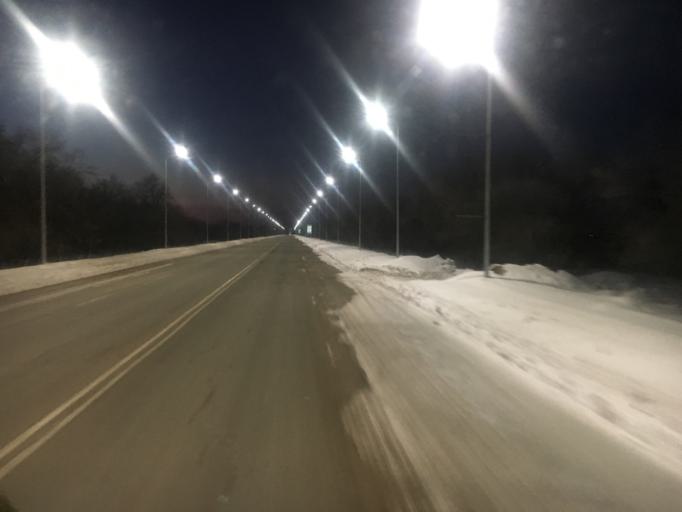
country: KZ
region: Batys Qazaqstan
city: Oral
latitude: 51.1576
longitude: 51.5336
